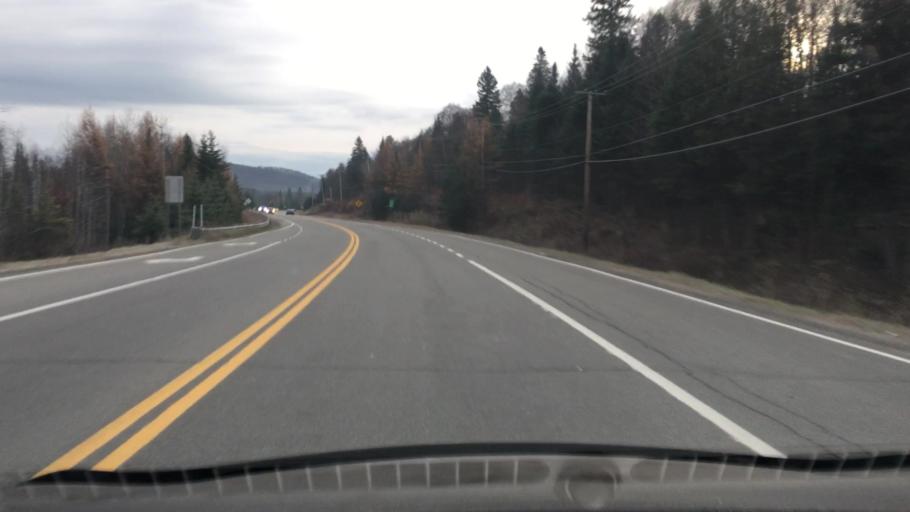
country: CA
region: Quebec
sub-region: Laurentides
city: Saint-Sauveur
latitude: 45.9002
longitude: -74.2230
